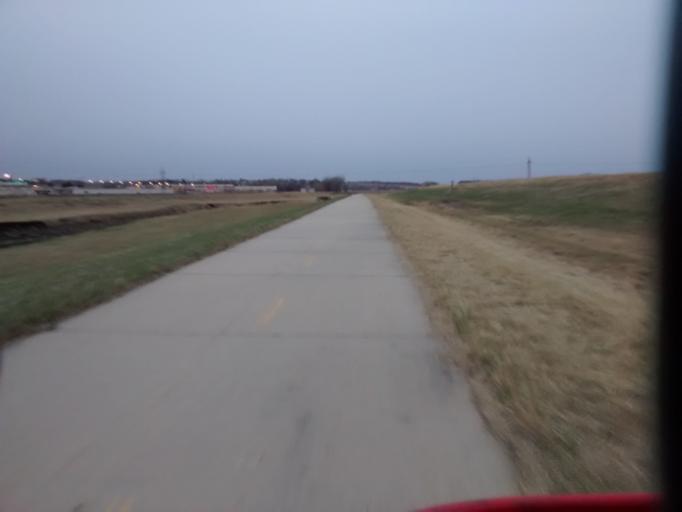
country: US
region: Nebraska
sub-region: Sarpy County
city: Offutt Air Force Base
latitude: 41.1443
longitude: -95.9586
